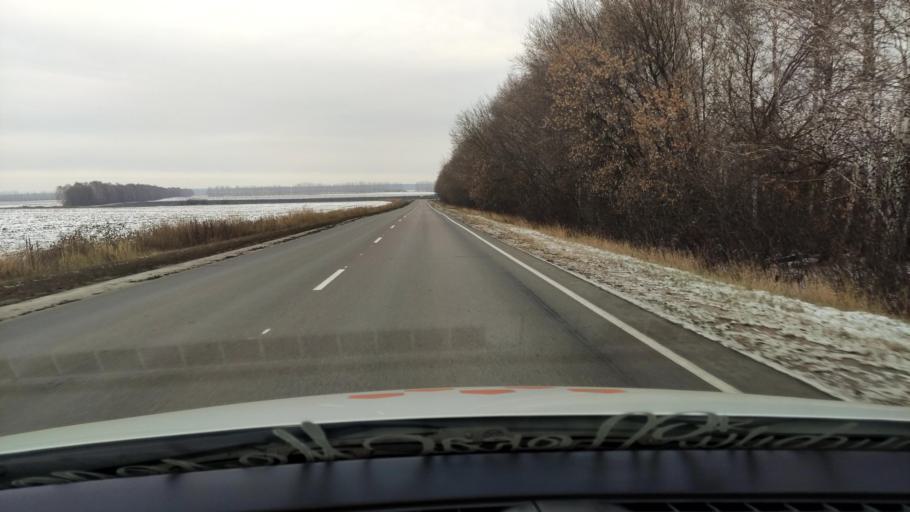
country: RU
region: Voronezj
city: Podgornoye
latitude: 51.8943
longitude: 39.1407
